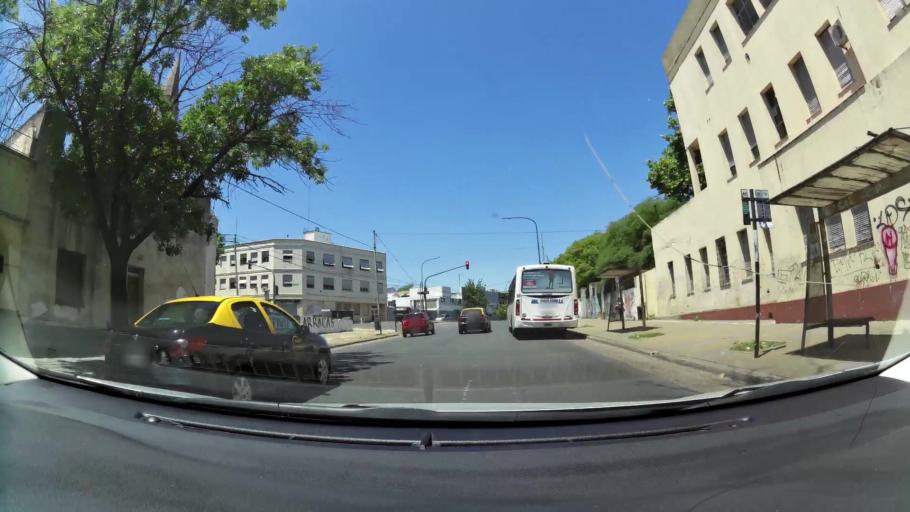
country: AR
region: Buenos Aires F.D.
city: Buenos Aires
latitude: -34.6339
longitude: -58.3829
